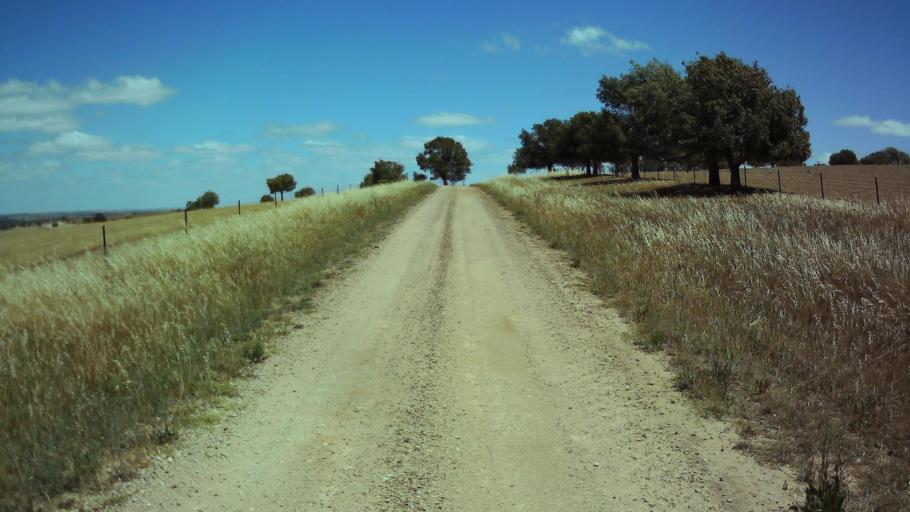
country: AU
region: New South Wales
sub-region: Weddin
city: Grenfell
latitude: -33.9663
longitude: 148.3625
